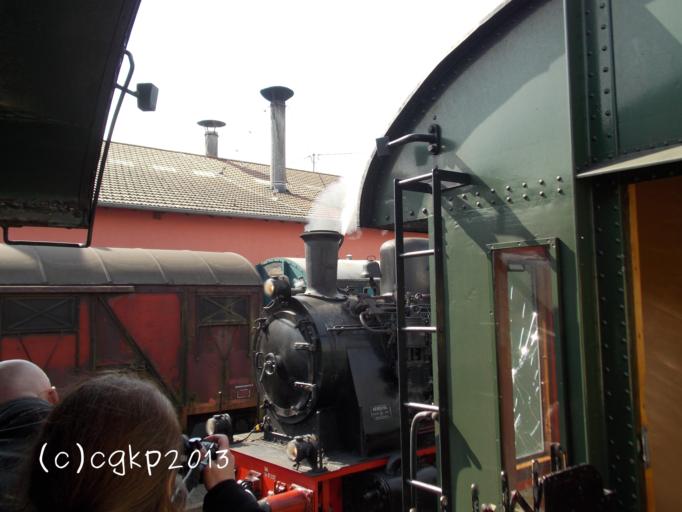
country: DE
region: Saarland
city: Losheim
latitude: 49.5063
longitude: 6.7456
